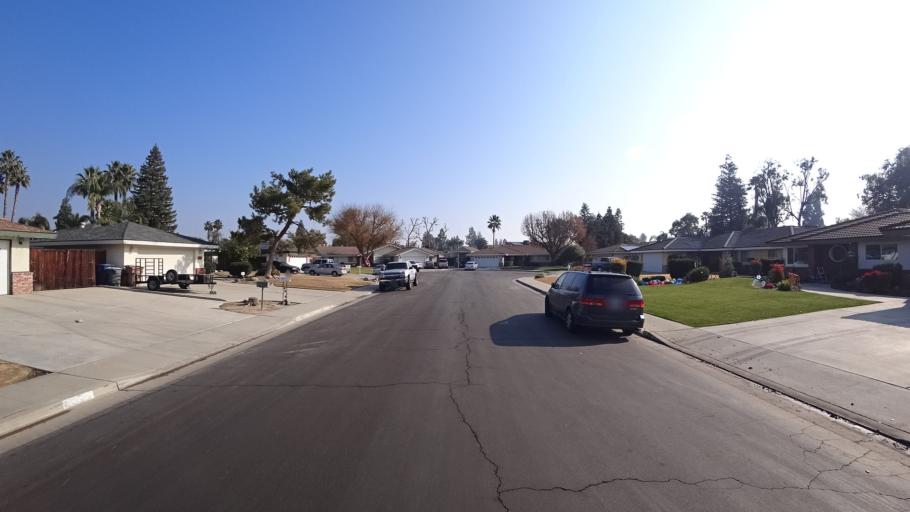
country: US
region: California
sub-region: Kern County
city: Greenacres
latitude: 35.3357
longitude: -119.0899
